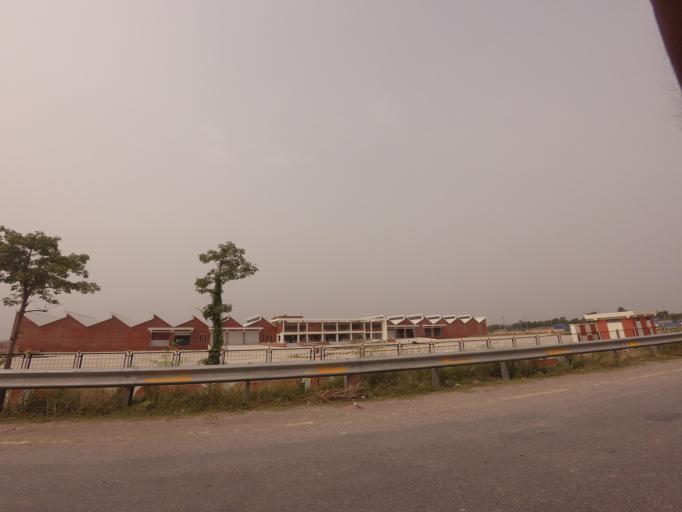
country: NP
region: Western Region
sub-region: Lumbini Zone
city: Bhairahawa
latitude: 27.5135
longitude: 83.3980
